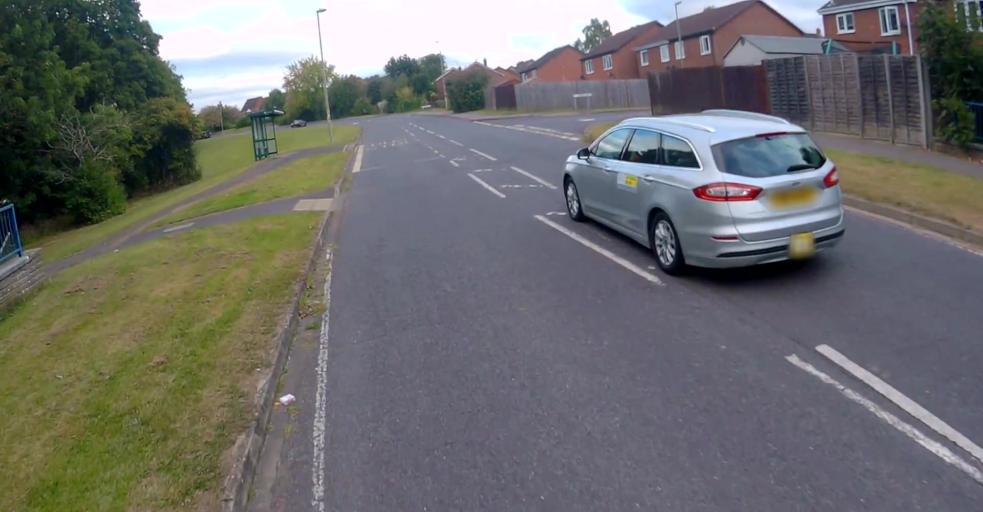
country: GB
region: England
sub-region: Hampshire
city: Basingstoke
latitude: 51.2421
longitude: -1.1246
